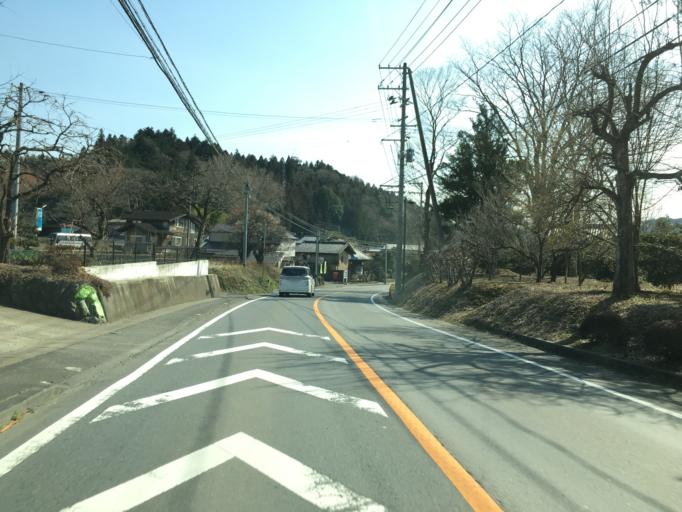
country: JP
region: Ibaraki
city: Daigo
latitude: 36.8773
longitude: 140.4233
